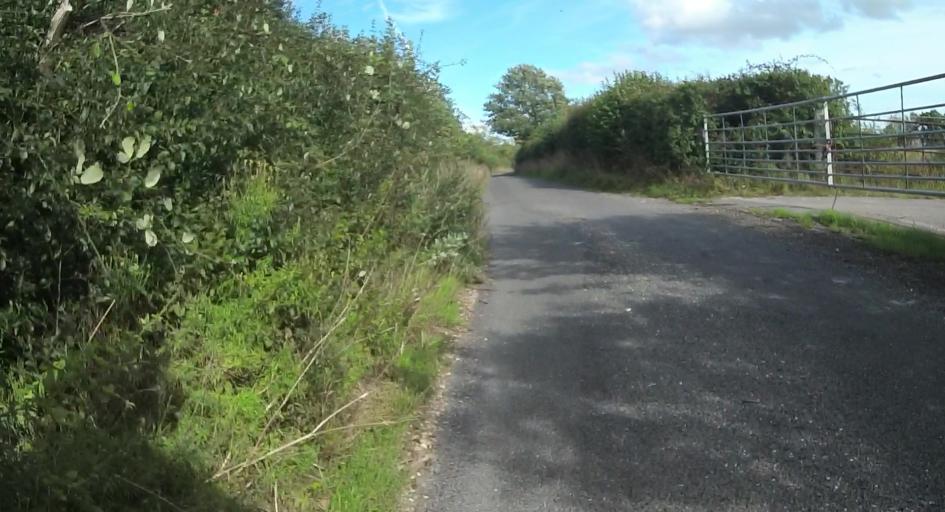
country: GB
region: England
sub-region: Hampshire
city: Kingsclere
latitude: 51.3636
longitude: -1.1942
